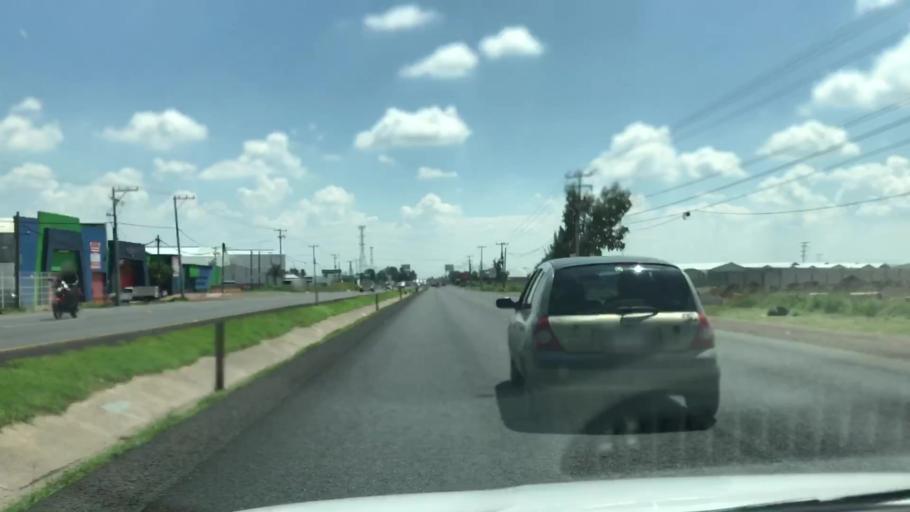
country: MX
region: Guanajuato
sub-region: Irapuato
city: Fraccionamiento las Liebres
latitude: 20.6363
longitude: -101.3853
